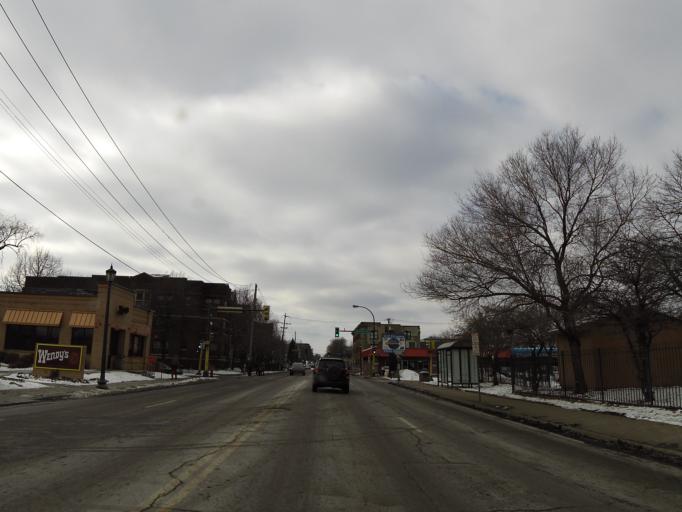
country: US
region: Minnesota
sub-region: Hennepin County
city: Minneapolis
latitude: 44.9627
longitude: -93.2708
